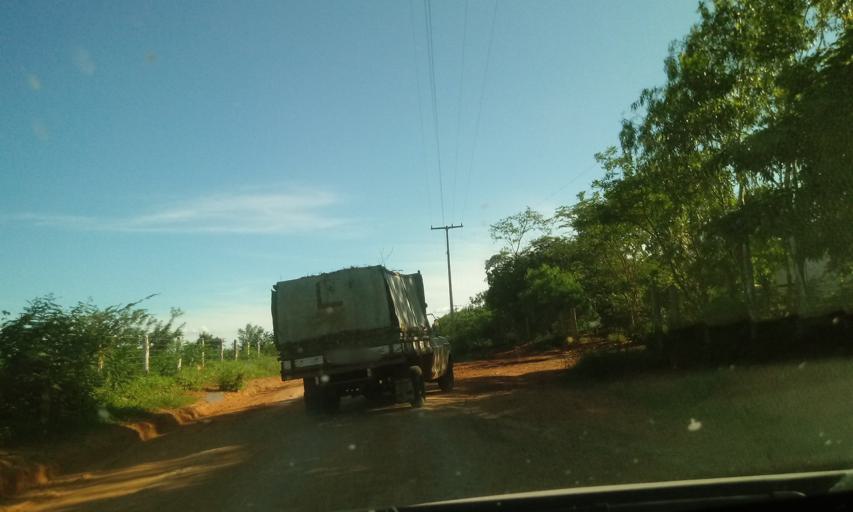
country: BR
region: Bahia
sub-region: Riacho De Santana
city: Riacho de Santana
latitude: -13.7817
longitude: -42.7233
